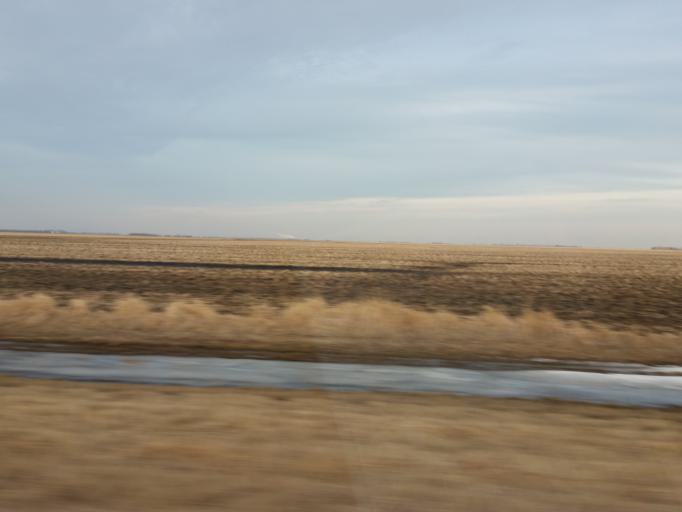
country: US
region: North Dakota
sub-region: Traill County
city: Mayville
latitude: 47.4095
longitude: -97.3262
